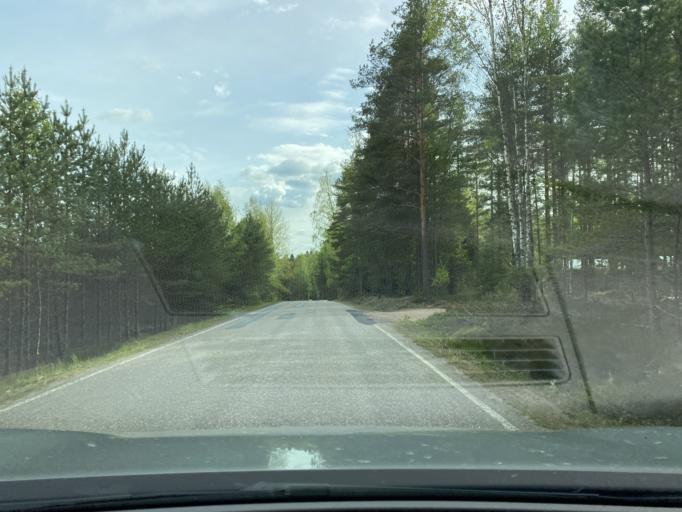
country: FI
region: Varsinais-Suomi
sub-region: Salo
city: Kiikala
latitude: 60.4902
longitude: 23.5507
